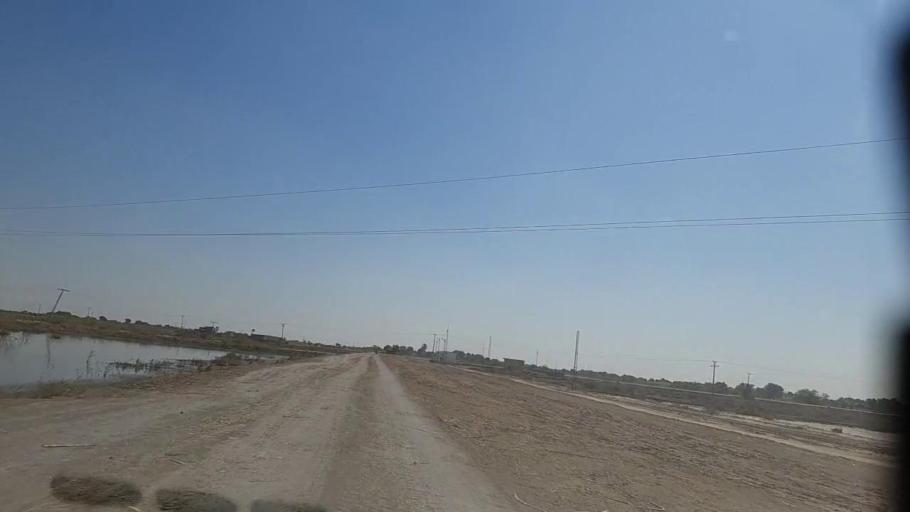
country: PK
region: Sindh
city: Digri
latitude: 25.1596
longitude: 69.0425
